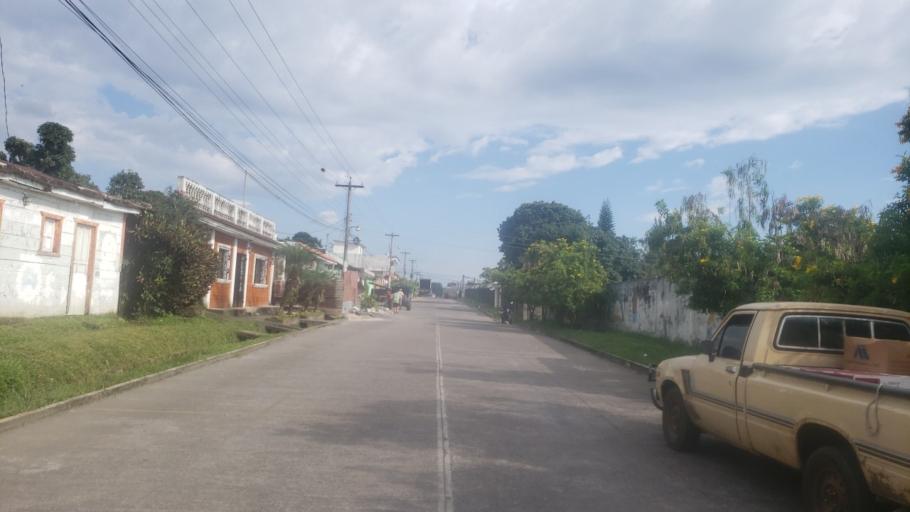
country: GT
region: Suchitepeque
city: Pueblo Nuevo
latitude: 14.6480
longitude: -91.5561
